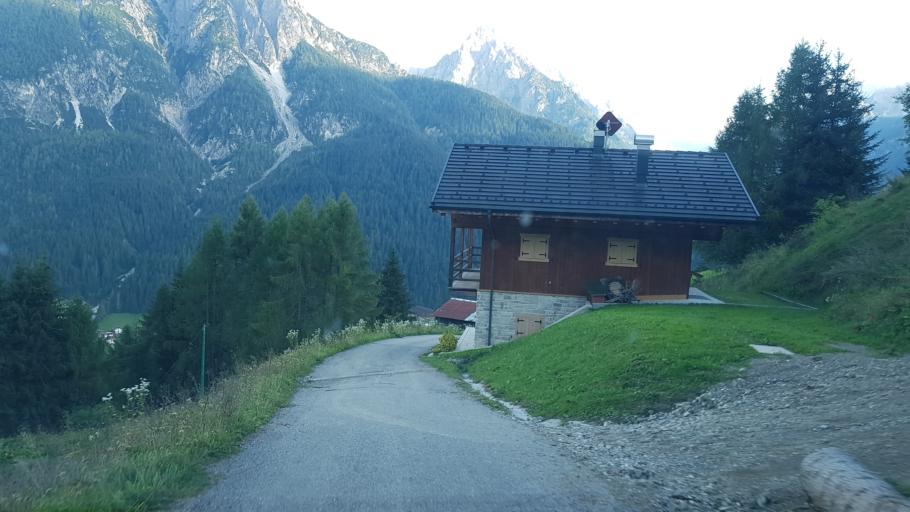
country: IT
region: Veneto
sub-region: Provincia di Belluno
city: San Pietro di Cadore
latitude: 46.5834
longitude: 12.5946
